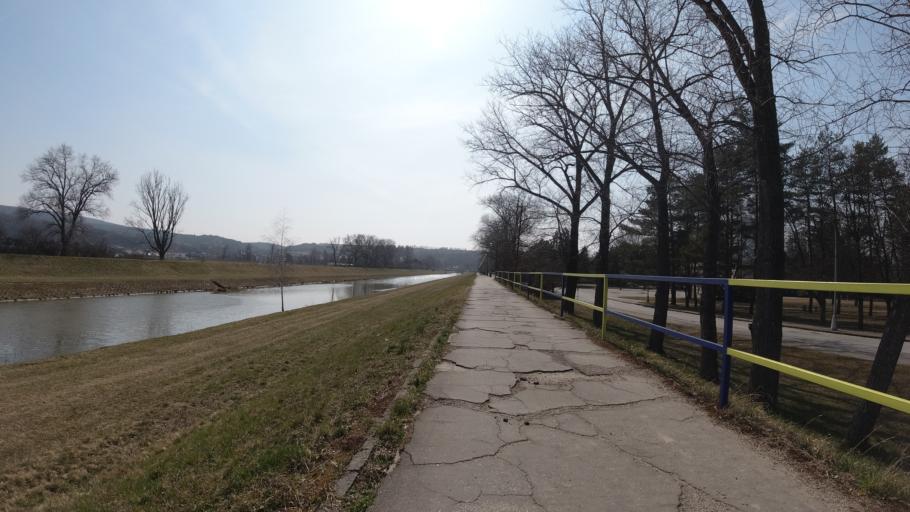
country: SK
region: Trnavsky
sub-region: Okres Trnava
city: Piestany
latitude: 48.5938
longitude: 17.8513
